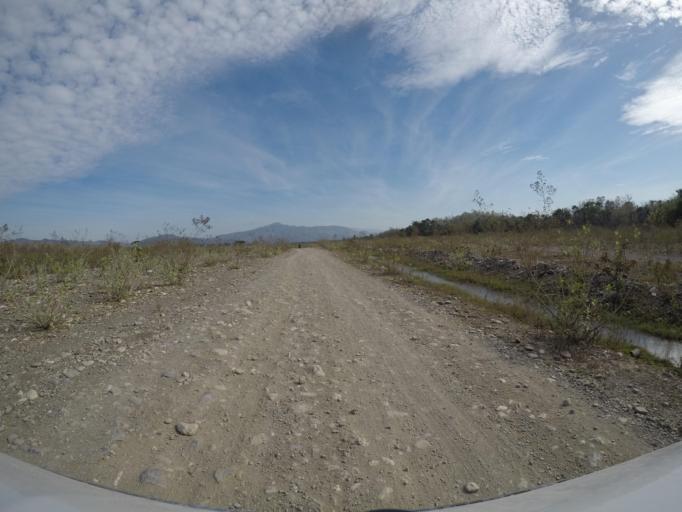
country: TL
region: Bobonaro
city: Maliana
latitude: -8.8976
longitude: 125.2090
